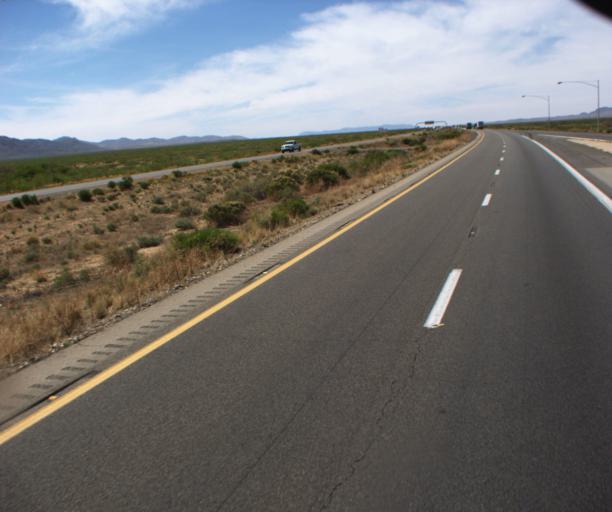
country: US
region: Arizona
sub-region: Cochise County
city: Willcox
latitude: 32.3326
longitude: -109.5196
